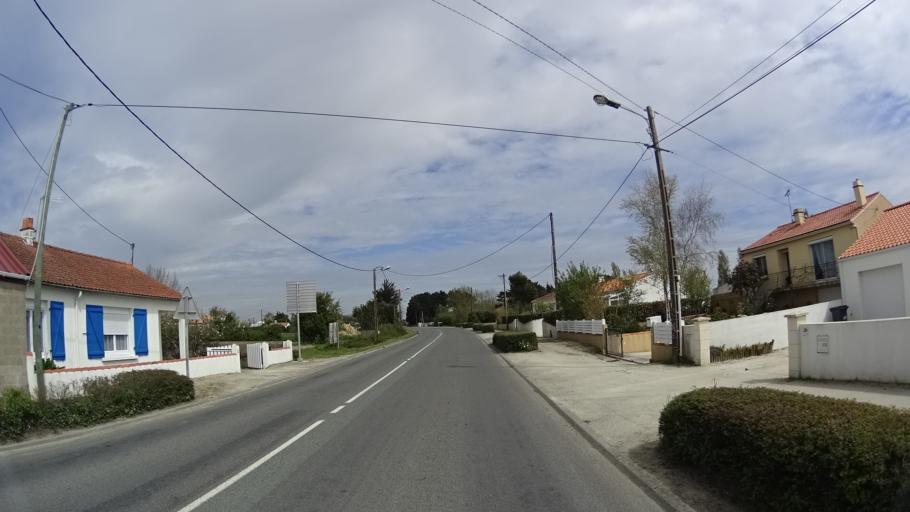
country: FR
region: Pays de la Loire
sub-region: Departement de la Vendee
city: Beauvoir-sur-Mer
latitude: 46.9195
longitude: -2.0432
